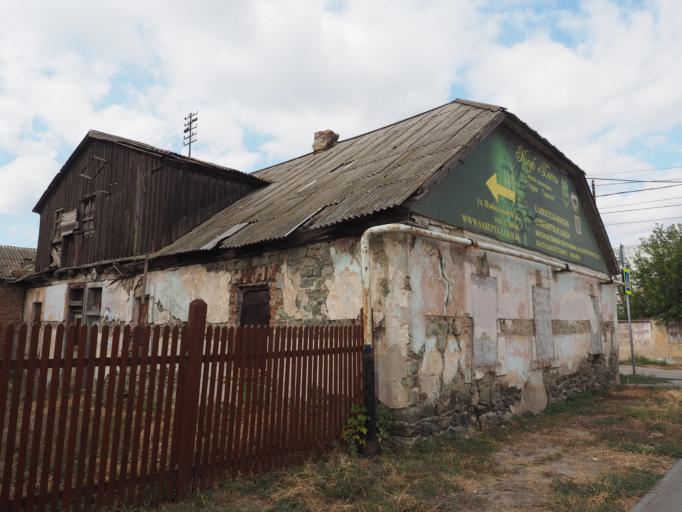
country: RU
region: Volgograd
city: Krasnoslobodsk
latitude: 48.5111
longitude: 44.5508
